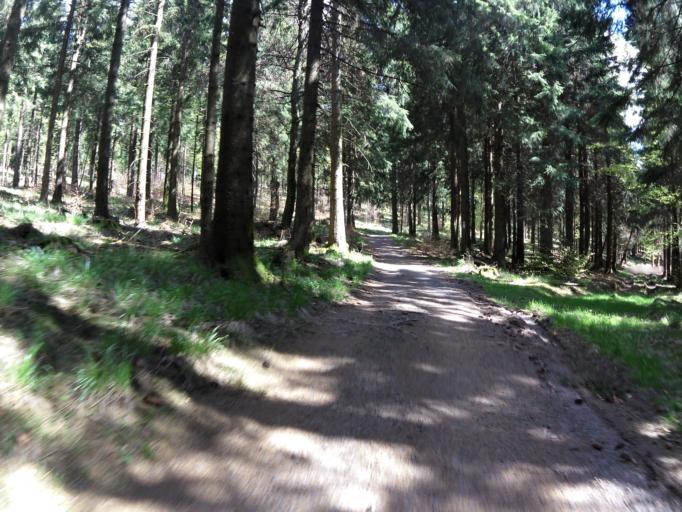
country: DE
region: Thuringia
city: Finsterbergen
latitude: 50.8070
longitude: 10.5436
